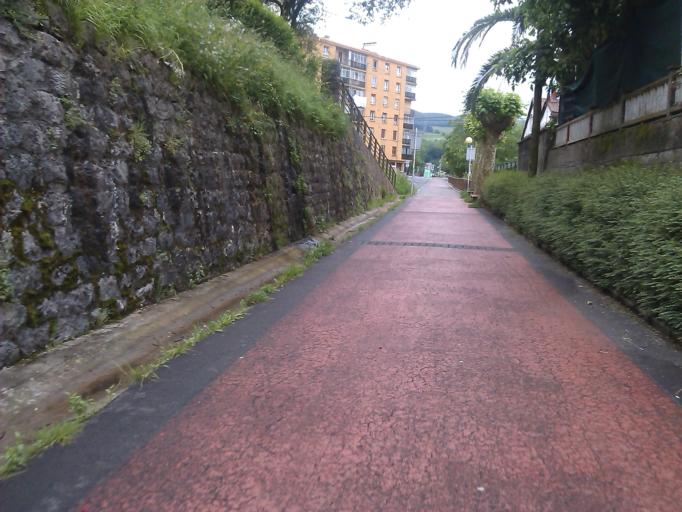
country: ES
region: Basque Country
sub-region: Provincia de Guipuzcoa
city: Andoain
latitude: 43.2181
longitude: -2.0194
